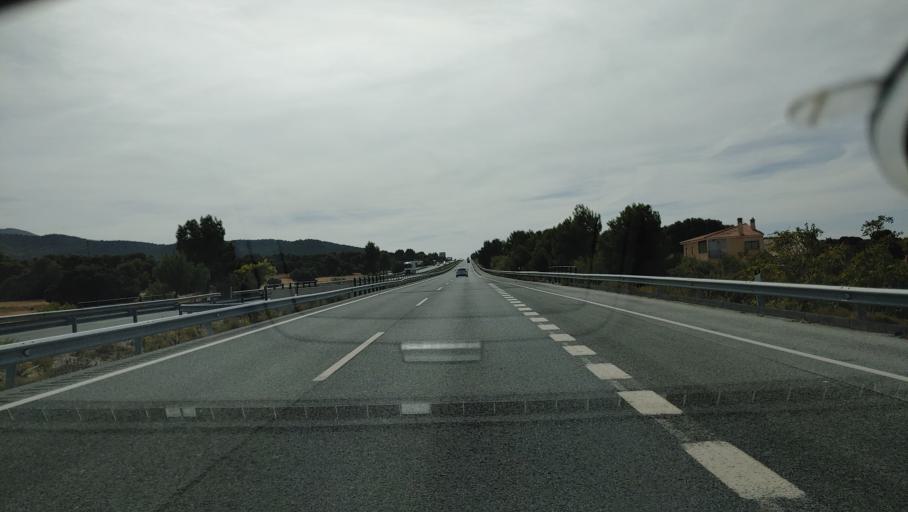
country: ES
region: Andalusia
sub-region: Provincia de Granada
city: Freila
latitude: 37.4456
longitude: -2.8897
